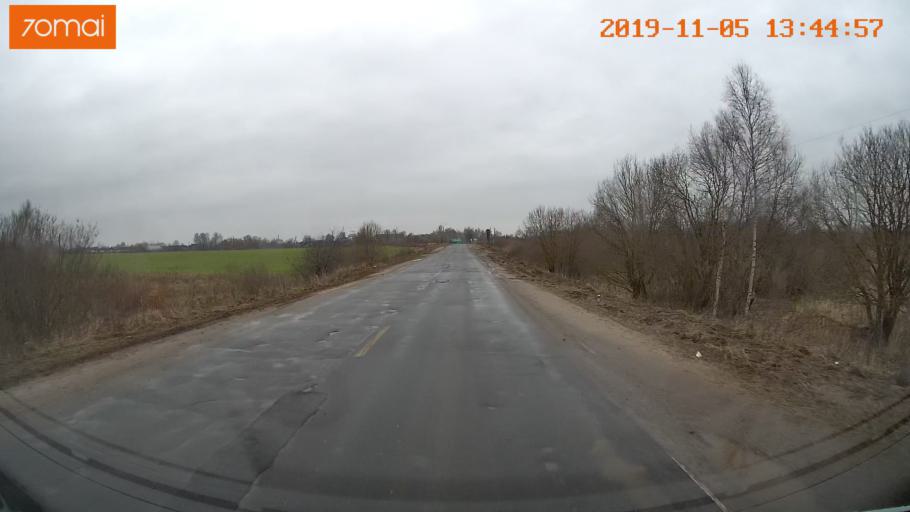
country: RU
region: Ivanovo
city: Shuya
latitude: 56.9848
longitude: 41.4117
